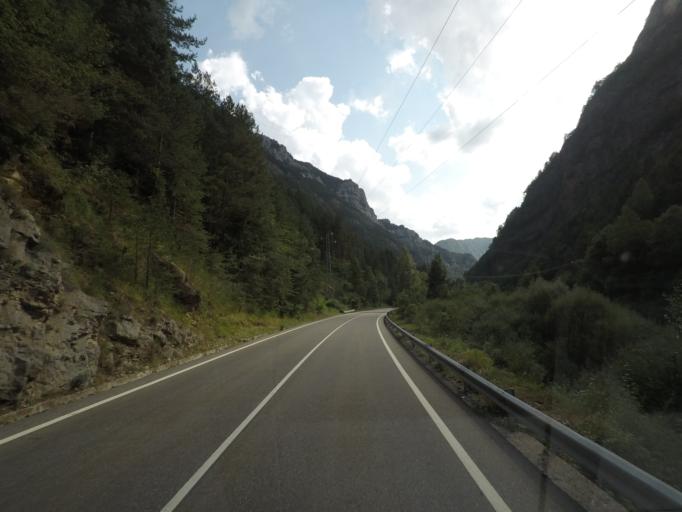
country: ES
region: Aragon
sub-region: Provincia de Huesca
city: Bielsa
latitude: 42.6011
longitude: 0.2402
